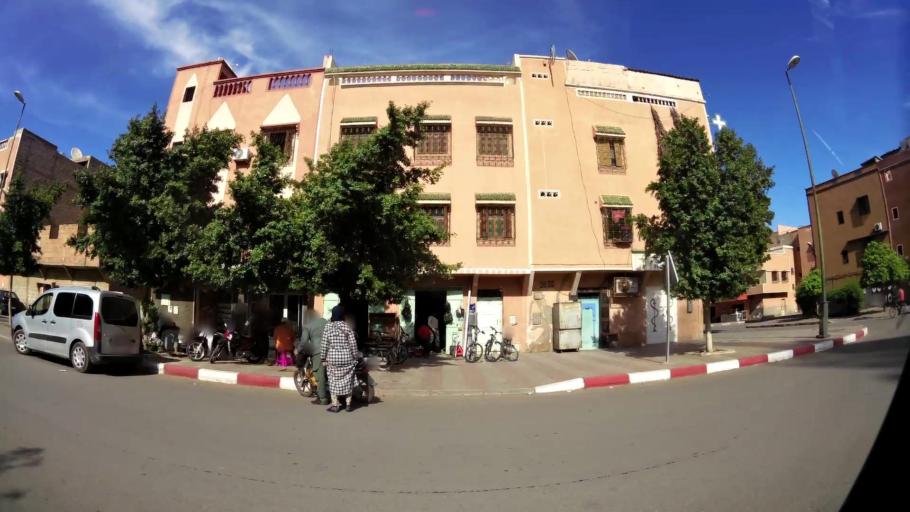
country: MA
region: Marrakech-Tensift-Al Haouz
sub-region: Marrakech
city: Marrakesh
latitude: 31.6072
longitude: -7.9608
